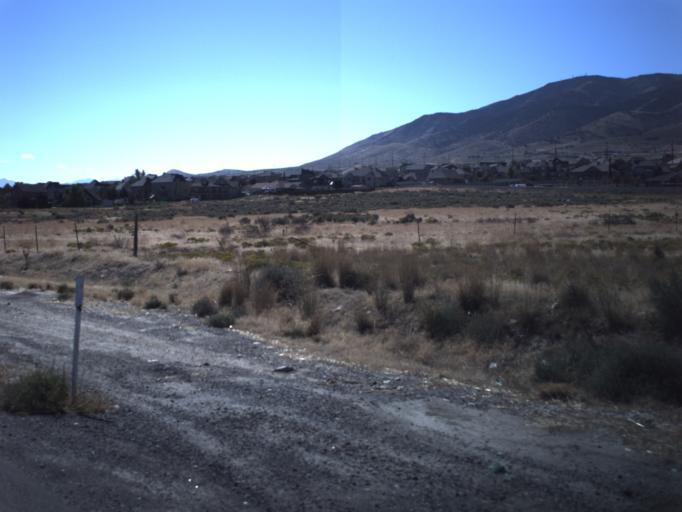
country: US
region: Utah
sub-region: Utah County
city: Saratoga Springs
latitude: 40.3259
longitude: -111.9054
